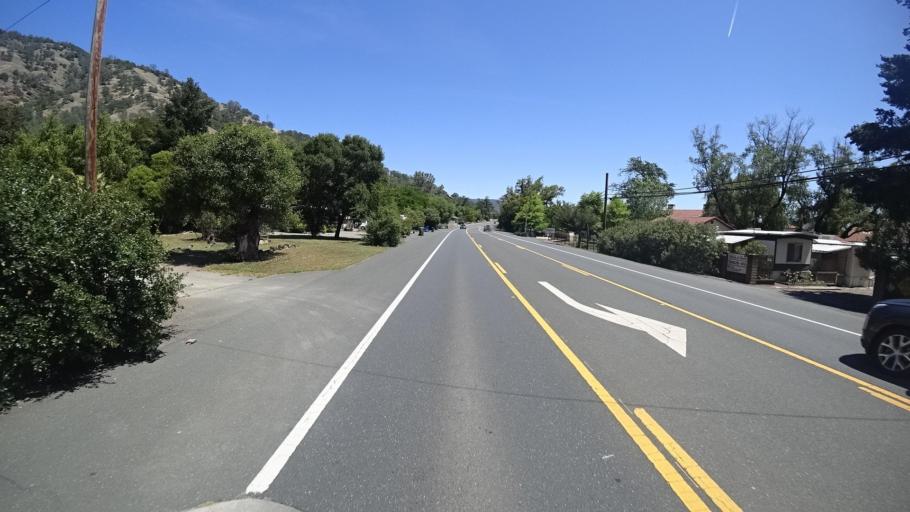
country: US
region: California
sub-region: Lake County
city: Nice
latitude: 39.1215
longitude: -122.8389
